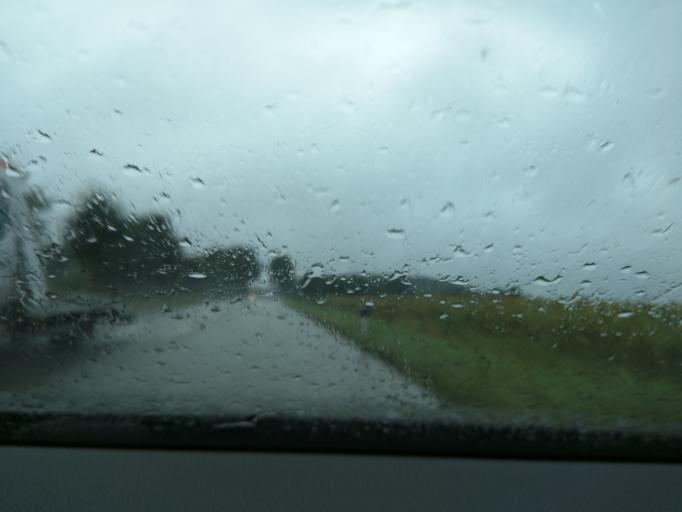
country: DE
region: Schleswig-Holstein
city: Grabau
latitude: 53.4829
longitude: 10.5271
